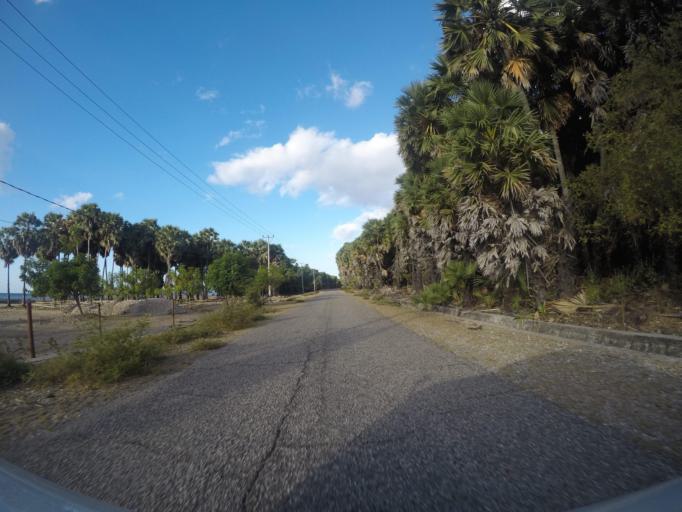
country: TL
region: Lautem
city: Lospalos
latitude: -8.3380
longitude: 126.9383
